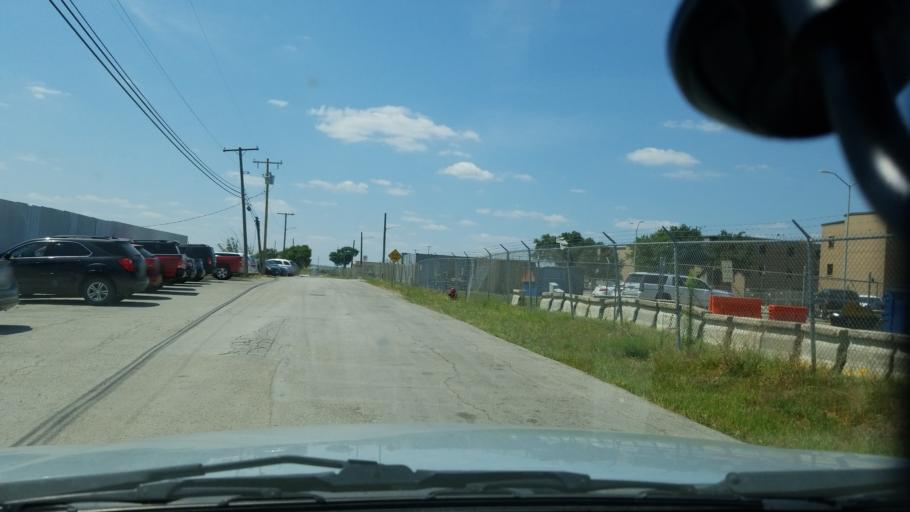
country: US
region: Texas
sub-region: Dallas County
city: Grand Prairie
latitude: 32.7415
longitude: -96.9533
